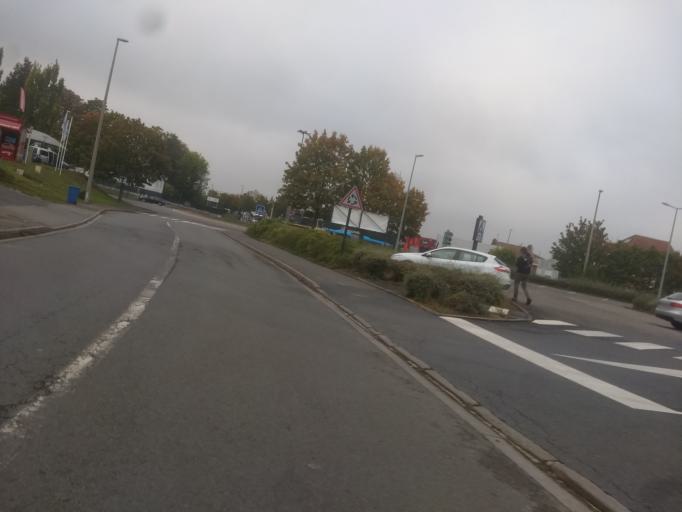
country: FR
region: Nord-Pas-de-Calais
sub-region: Departement du Pas-de-Calais
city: Arras
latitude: 50.2920
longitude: 2.7941
